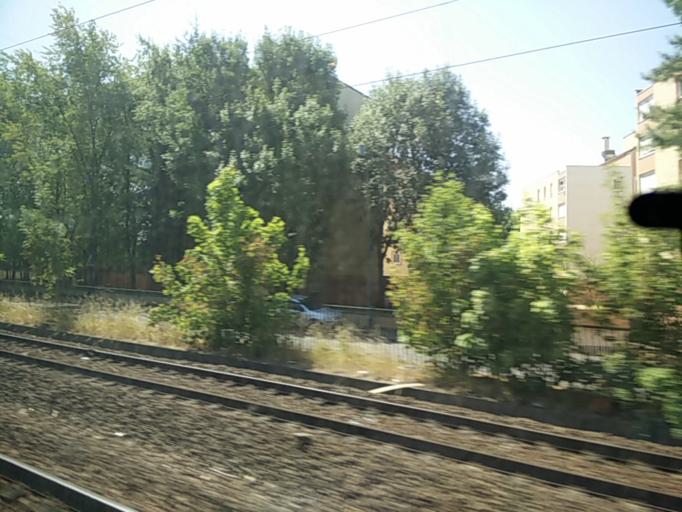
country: FR
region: Ile-de-France
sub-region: Departement de Seine-et-Marne
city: Roissy-en-Brie
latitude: 48.7971
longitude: 2.6464
